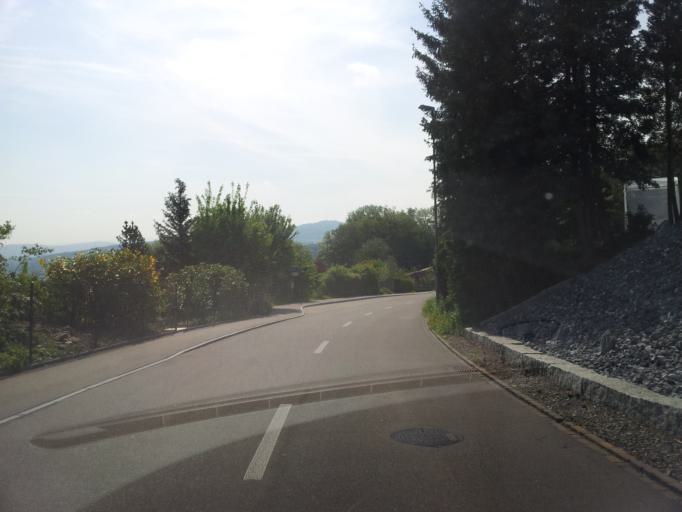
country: CH
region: Zurich
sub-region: Bezirk Dietikon
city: Dietikon / Oberdorf
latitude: 47.3947
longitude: 8.3797
